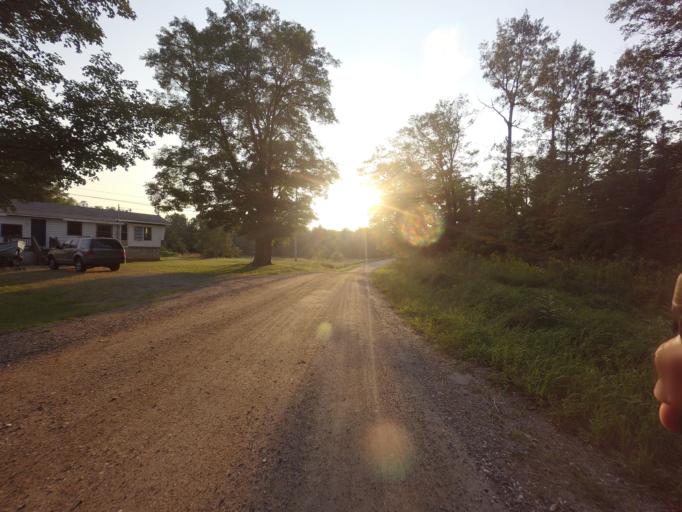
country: CA
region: Ontario
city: Renfrew
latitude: 45.0654
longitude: -76.7581
